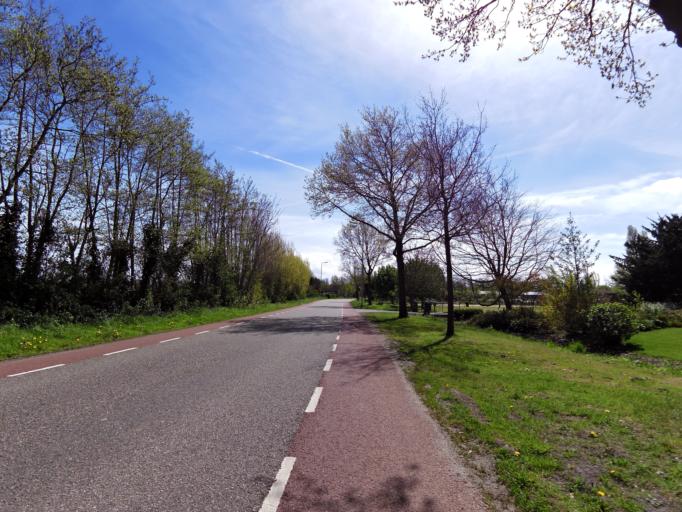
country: NL
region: South Holland
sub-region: Gemeente Hellevoetsluis
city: Nieuwenhoorn
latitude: 51.8948
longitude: 4.0891
